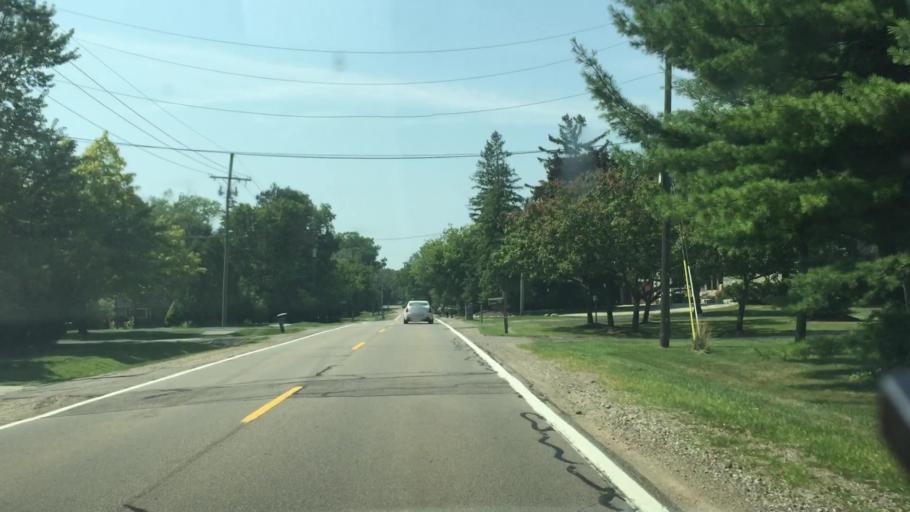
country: US
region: Michigan
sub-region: Oakland County
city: Franklin
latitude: 42.5533
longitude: -83.3282
